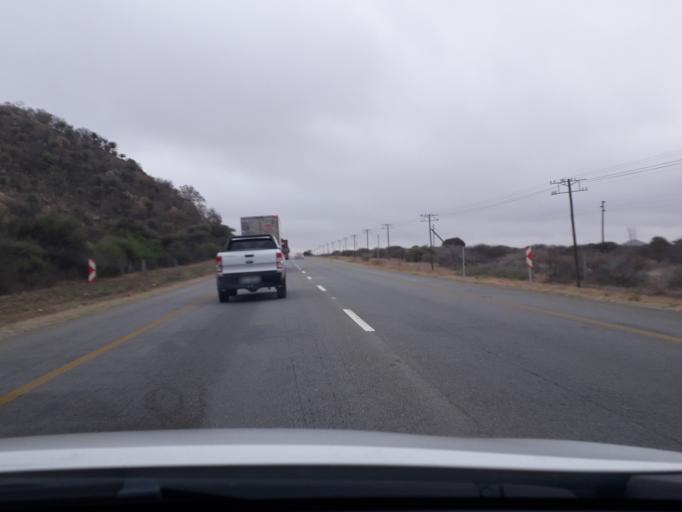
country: ZA
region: Limpopo
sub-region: Capricorn District Municipality
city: Mankoeng
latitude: -23.5266
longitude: 29.7056
